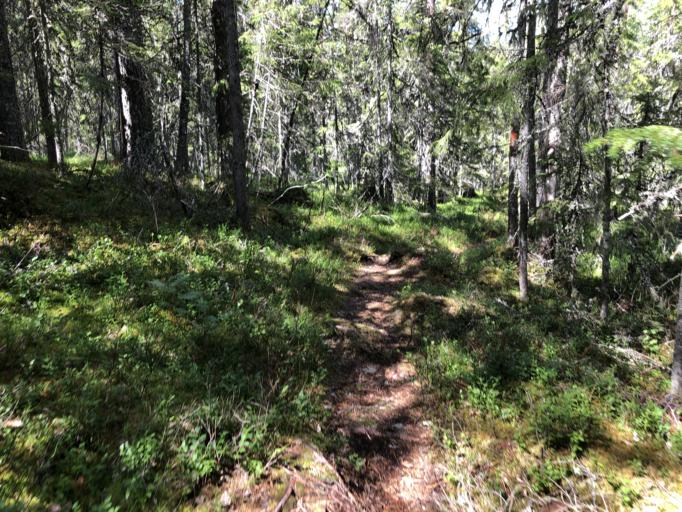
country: SE
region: Dalarna
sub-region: Vansbro Kommun
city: Jarna
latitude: 60.6670
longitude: 14.2718
